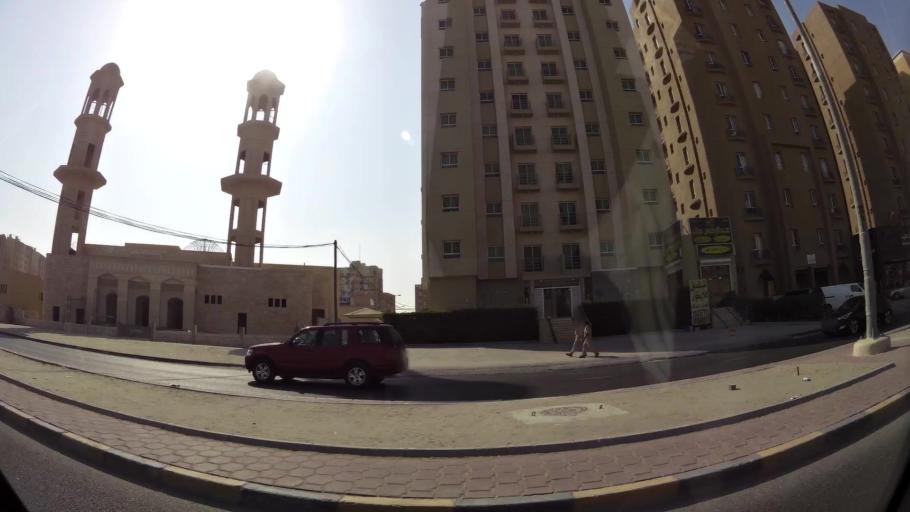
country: KW
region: Al Ahmadi
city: Al Mahbulah
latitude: 29.1540
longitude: 48.1163
